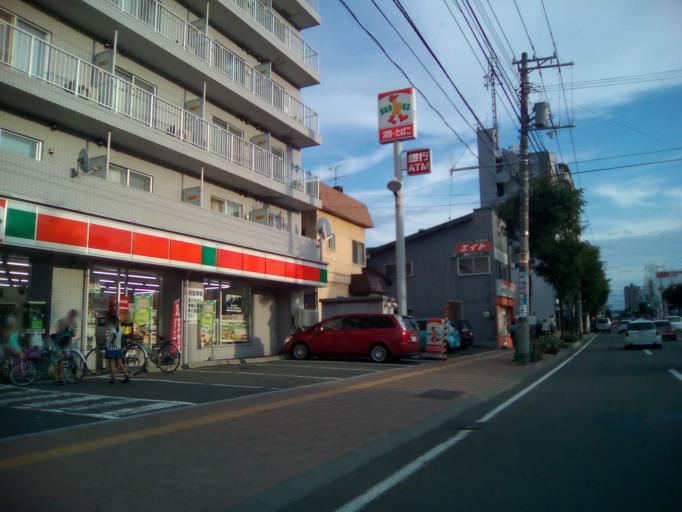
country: JP
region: Hokkaido
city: Sapporo
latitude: 43.0191
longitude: 141.3670
